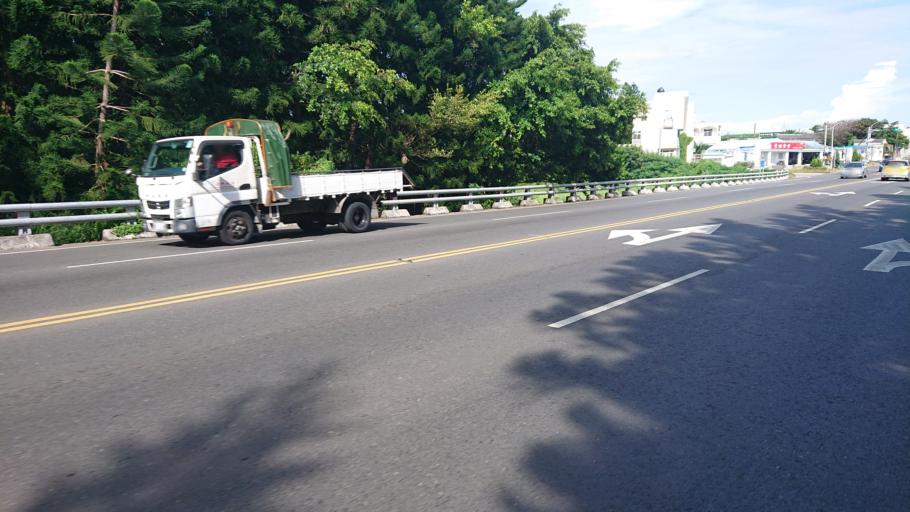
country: TW
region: Taiwan
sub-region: Penghu
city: Ma-kung
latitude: 23.5531
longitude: 119.6098
